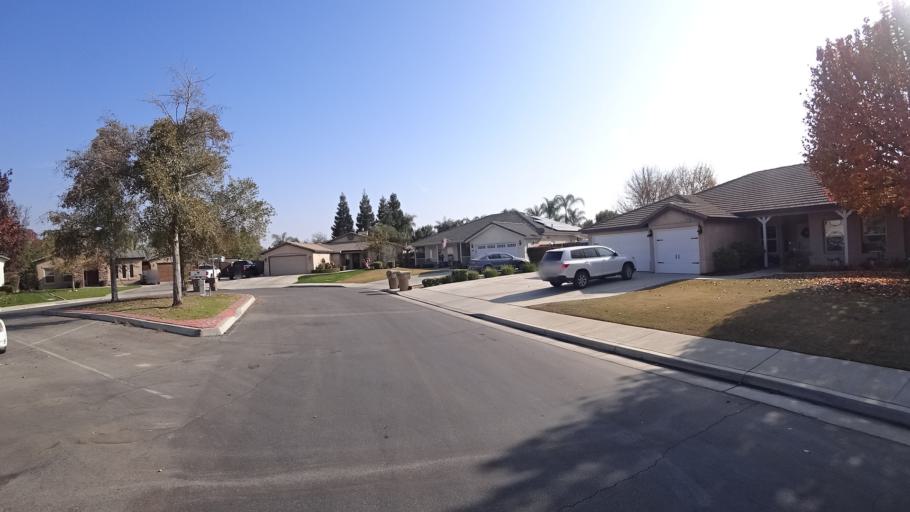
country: US
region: California
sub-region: Kern County
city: Greenacres
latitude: 35.4256
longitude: -119.1121
